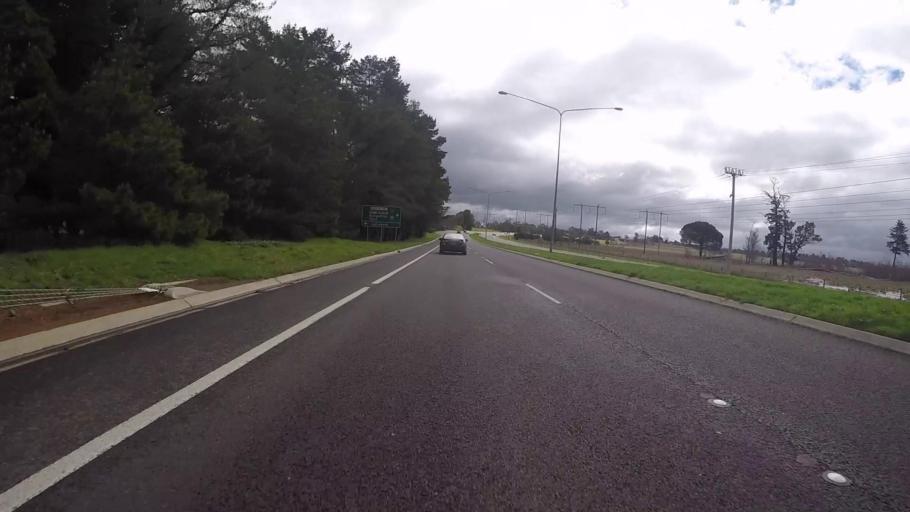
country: AU
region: Australian Capital Territory
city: Kaleen
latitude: -35.2341
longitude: 149.1279
